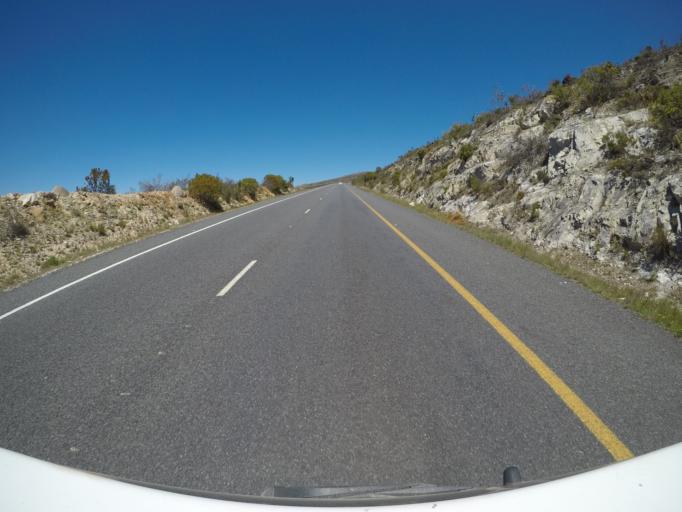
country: ZA
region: Western Cape
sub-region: Overberg District Municipality
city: Grabouw
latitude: -34.2198
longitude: 19.1848
